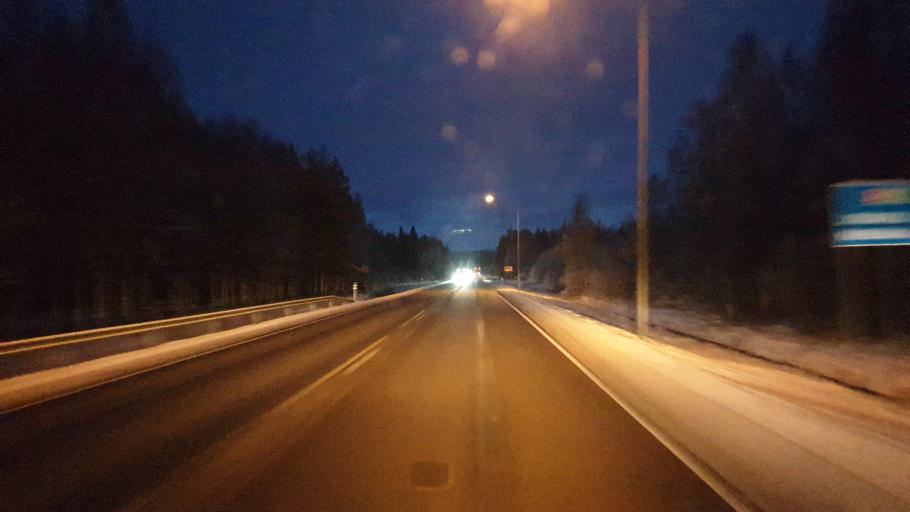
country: FI
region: Northern Ostrobothnia
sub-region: Haapavesi-Siikalatva
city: Pulkkila
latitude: 64.2610
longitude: 25.8654
